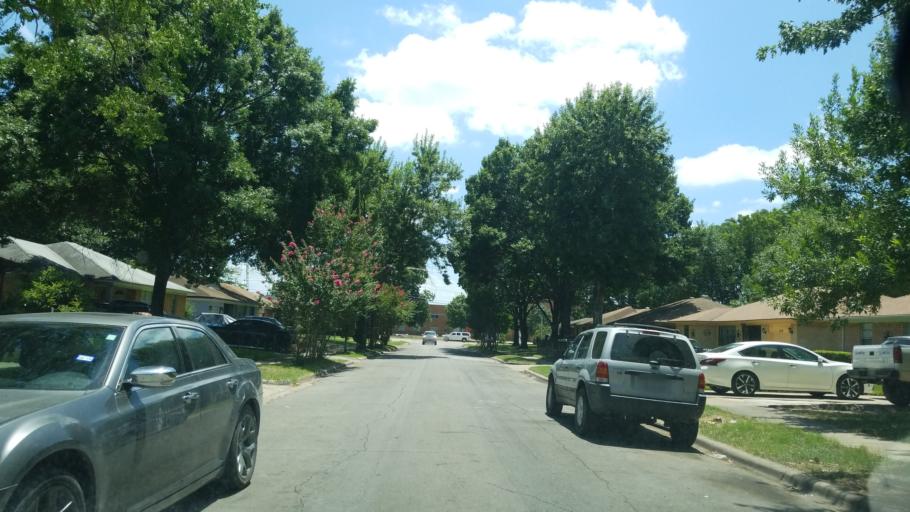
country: US
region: Texas
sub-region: Dallas County
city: Balch Springs
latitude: 32.7355
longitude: -96.7066
